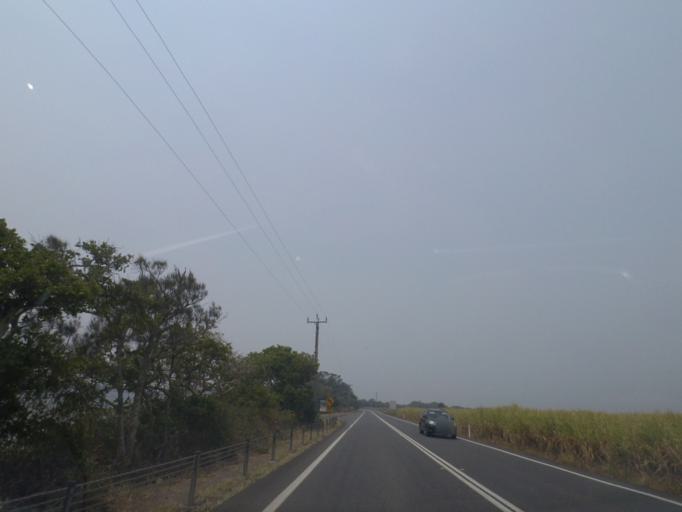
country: AU
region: New South Wales
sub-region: Richmond Valley
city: Evans Head
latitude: -28.9944
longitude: 153.4585
